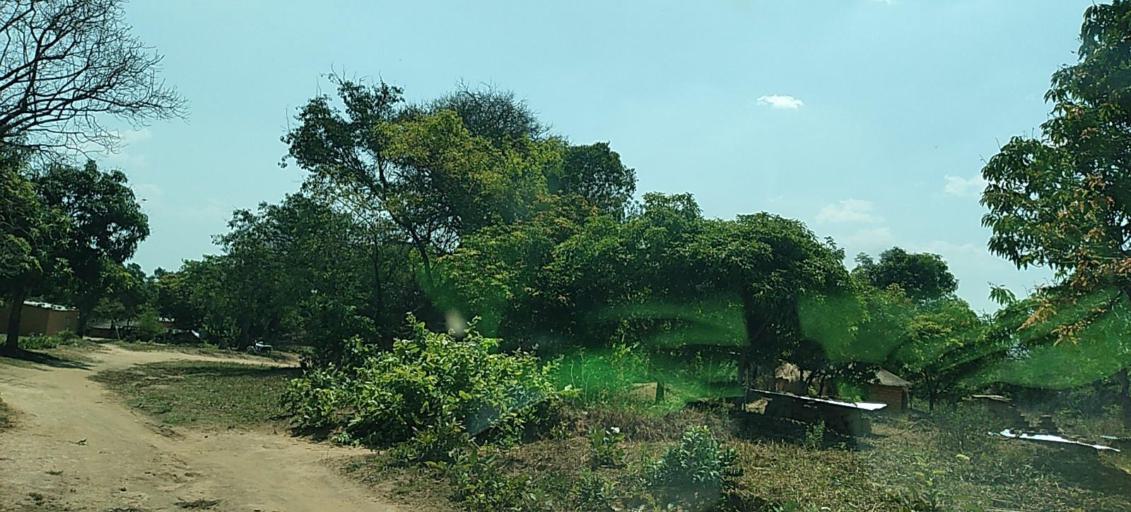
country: CD
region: Katanga
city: Kolwezi
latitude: -11.2821
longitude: 25.1481
